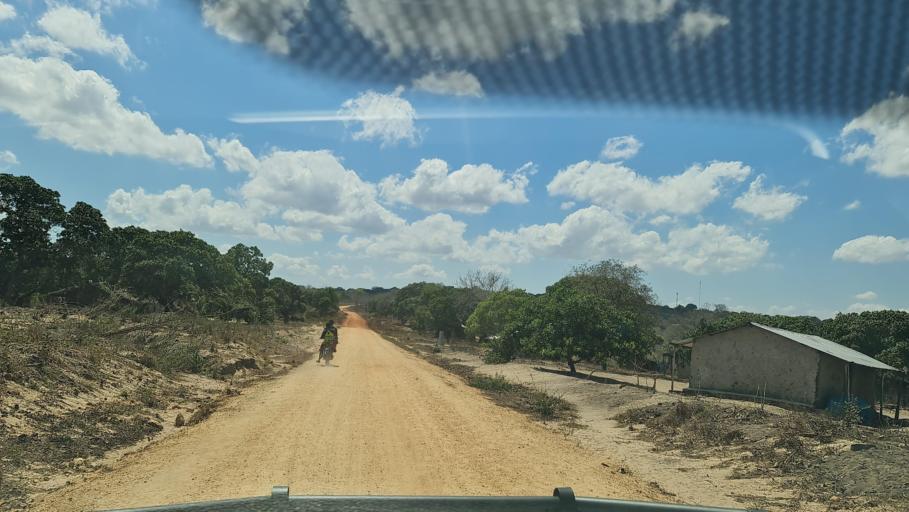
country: MZ
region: Nampula
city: Nacala
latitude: -14.1691
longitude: 40.2499
